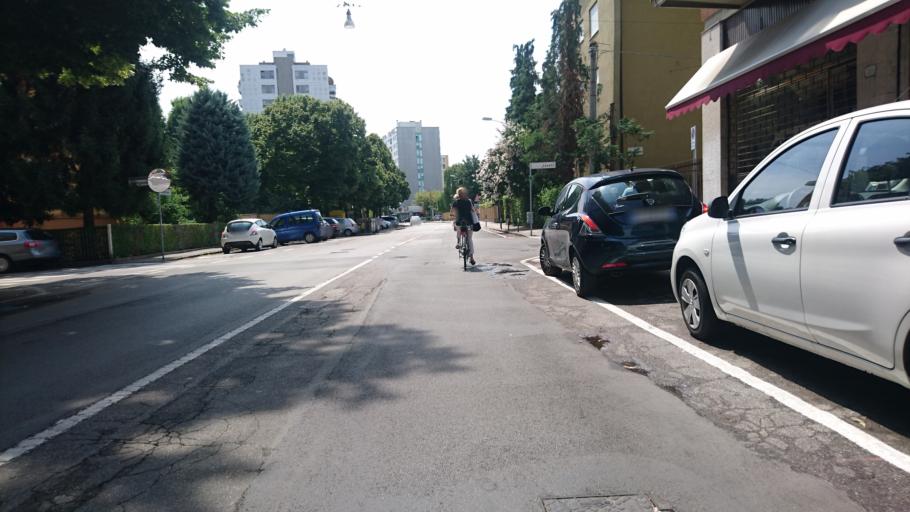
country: IT
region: Veneto
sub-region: Provincia di Padova
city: Padova
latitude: 45.3948
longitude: 11.8625
